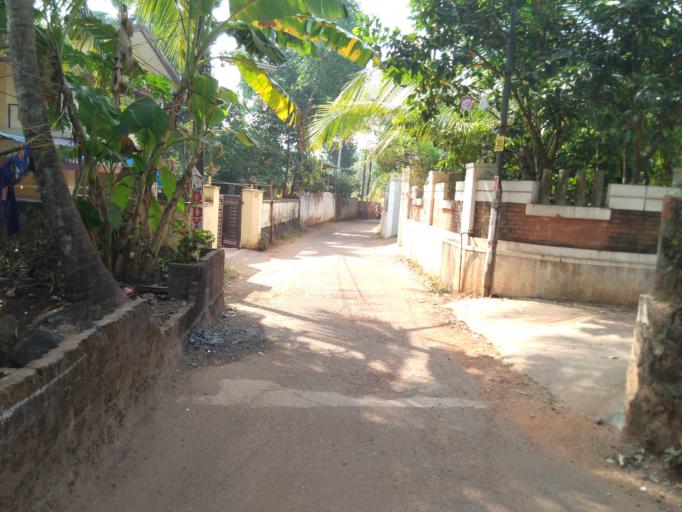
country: IN
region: Kerala
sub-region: Kozhikode
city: Kunnamangalam
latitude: 11.2924
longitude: 75.8290
